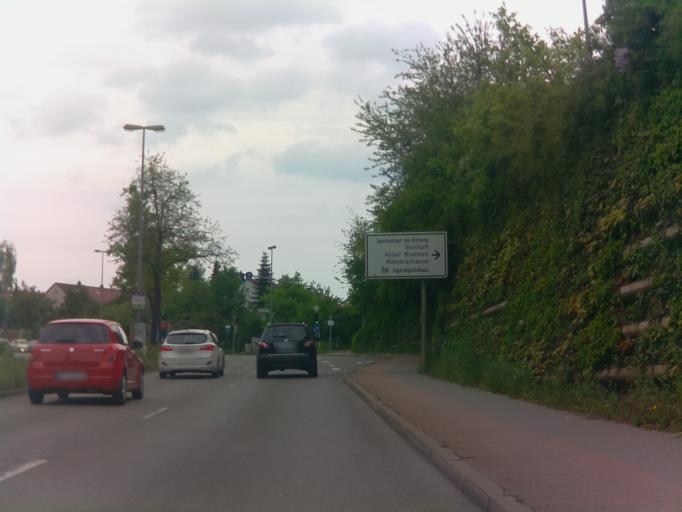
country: DE
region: Baden-Wuerttemberg
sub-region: Tuebingen Region
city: Reutlingen
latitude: 48.5047
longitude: 9.2063
